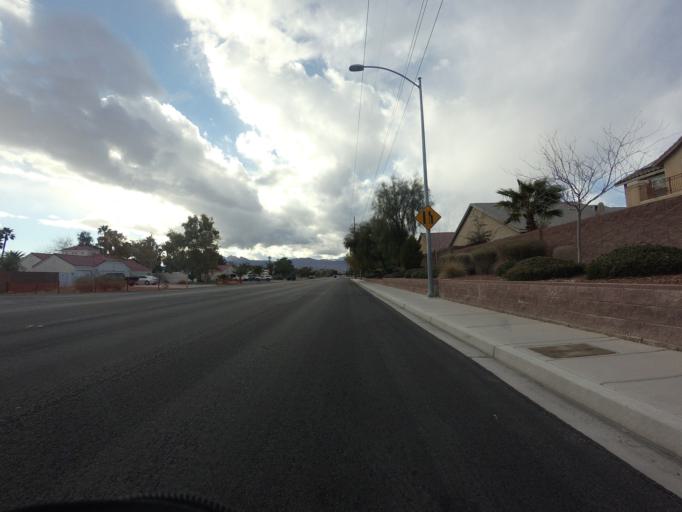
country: US
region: Nevada
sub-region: Clark County
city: Las Vegas
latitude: 36.2686
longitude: -115.2273
